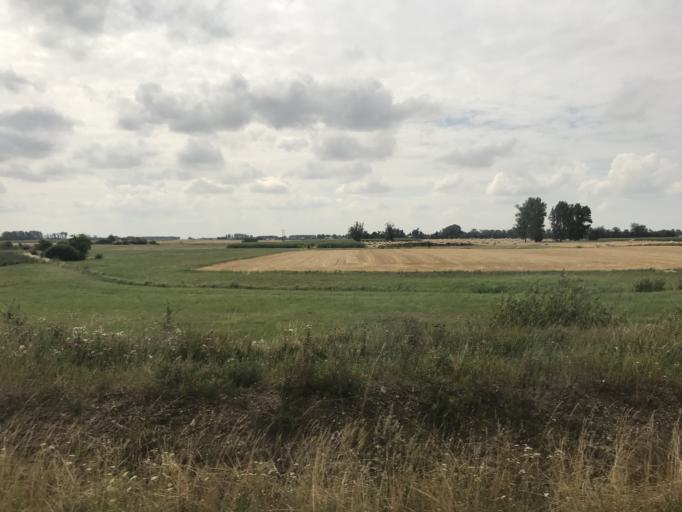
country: PL
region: Greater Poland Voivodeship
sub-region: Powiat gnieznienski
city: Niechanowo
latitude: 52.5337
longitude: 17.6723
